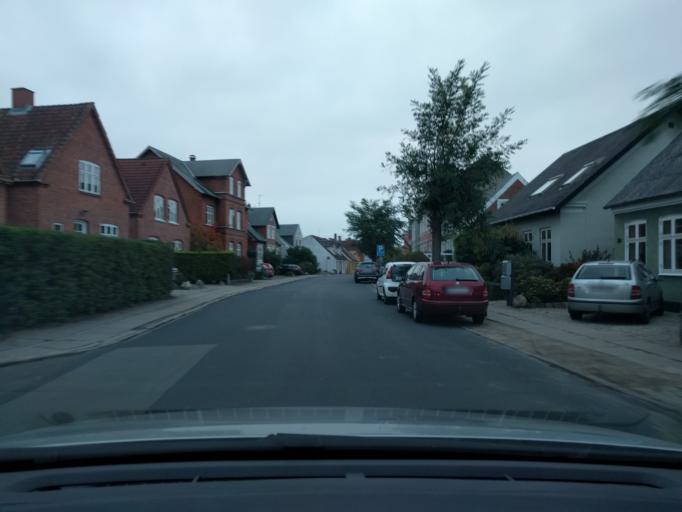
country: DK
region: South Denmark
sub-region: Svendborg Kommune
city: Svendborg
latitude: 55.0579
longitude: 10.5996
